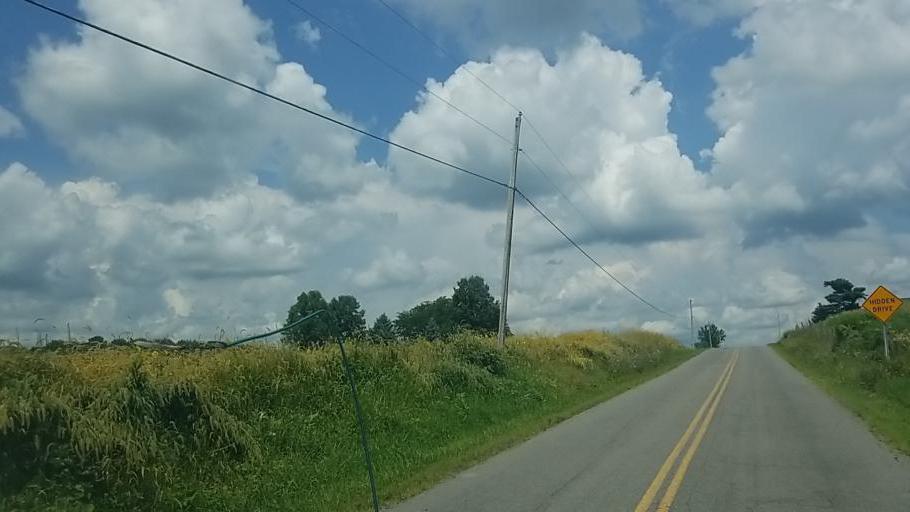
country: US
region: Ohio
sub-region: Medina County
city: Lodi
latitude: 41.0314
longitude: -82.0775
